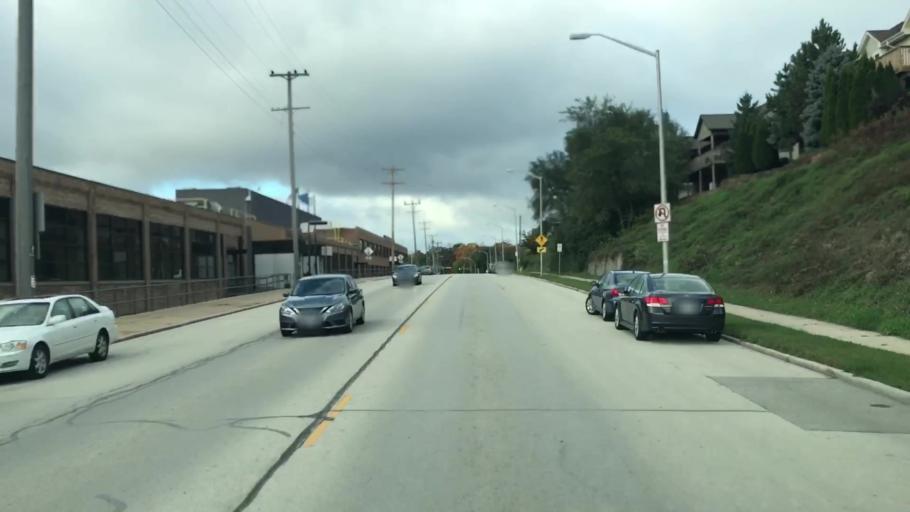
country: US
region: Wisconsin
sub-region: Waukesha County
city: Waukesha
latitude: 43.0062
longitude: -88.2475
